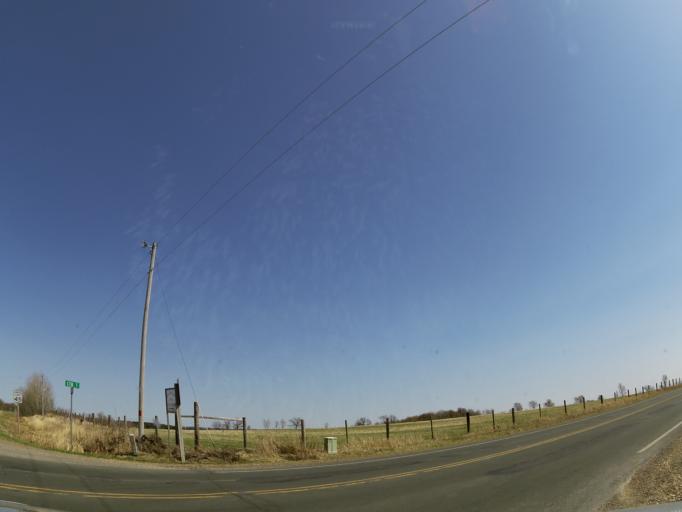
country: US
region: Wisconsin
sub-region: Saint Croix County
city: Hammond
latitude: 44.9343
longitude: -92.4354
